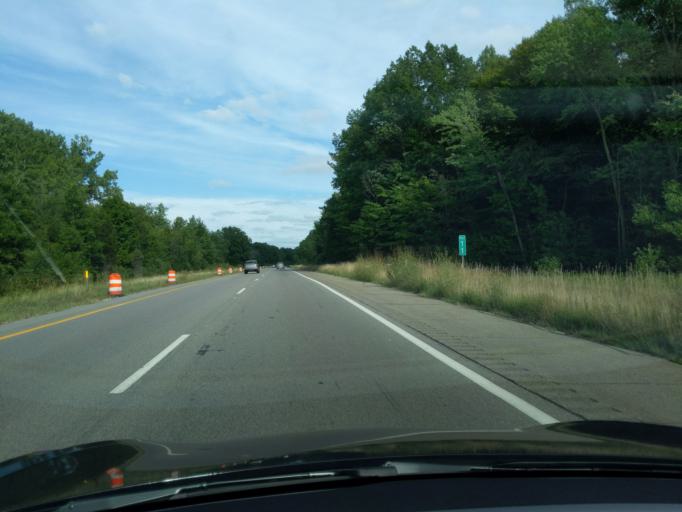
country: US
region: Michigan
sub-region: Ottawa County
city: Coopersville
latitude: 43.0735
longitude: -86.0494
